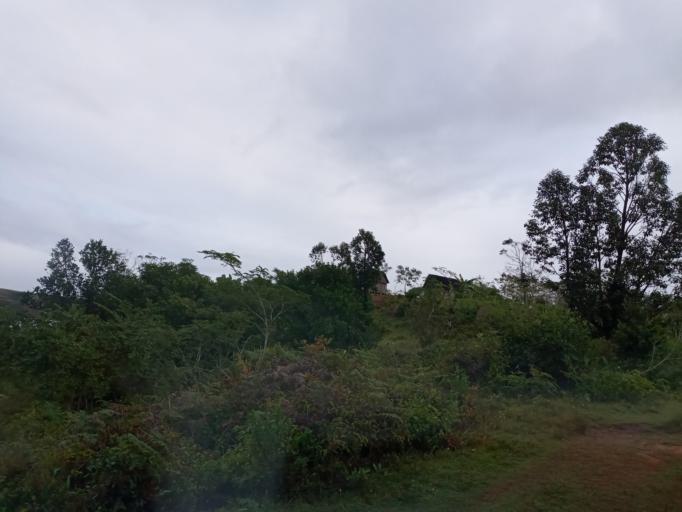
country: MG
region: Atsimo-Atsinanana
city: Vohipaho
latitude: -24.0129
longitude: 47.4158
